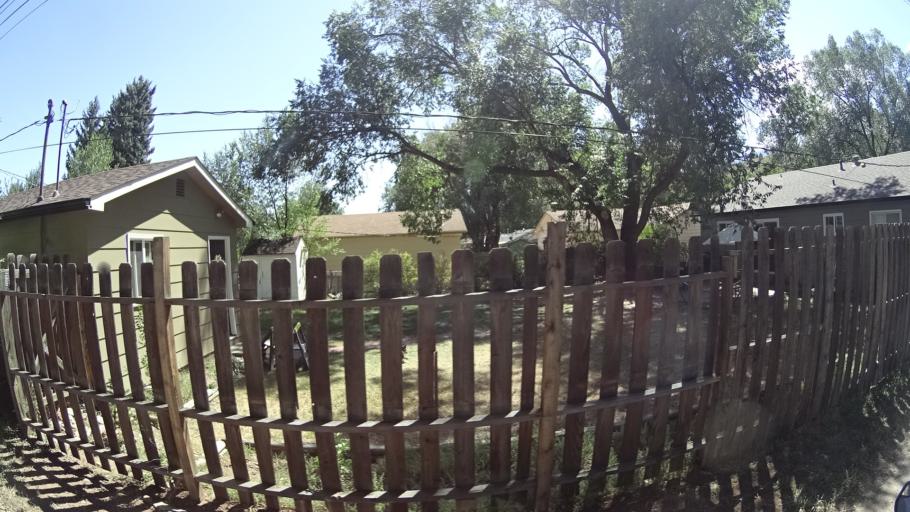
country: US
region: Colorado
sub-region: El Paso County
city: Manitou Springs
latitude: 38.8591
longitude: -104.8702
